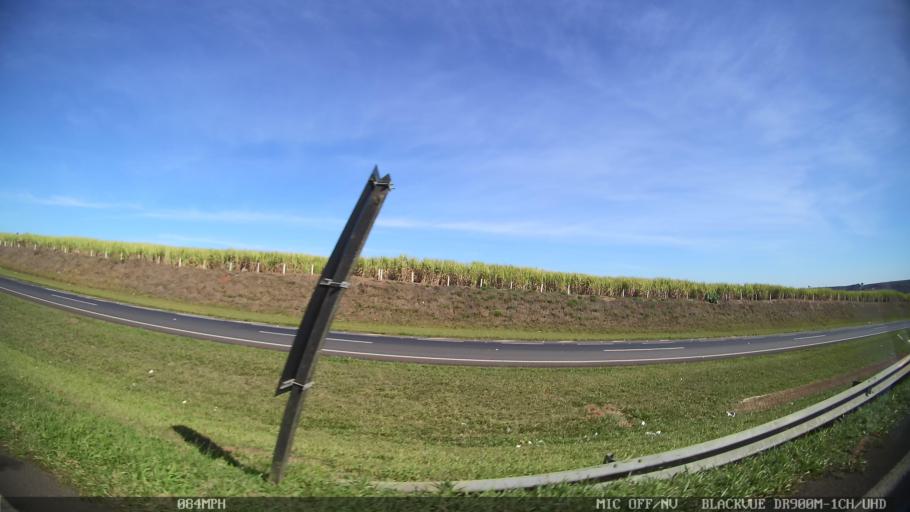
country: BR
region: Sao Paulo
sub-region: Leme
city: Leme
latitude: -22.1068
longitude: -47.4130
